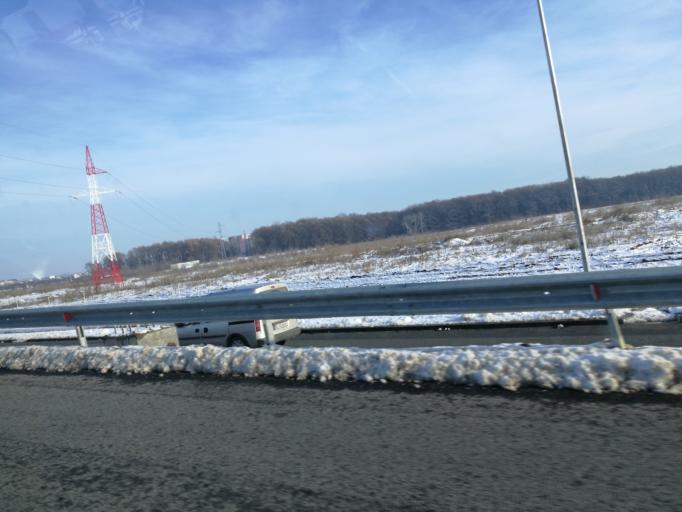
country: RO
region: Ilfov
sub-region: Voluntari City
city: Voluntari
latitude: 44.4901
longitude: 26.1472
